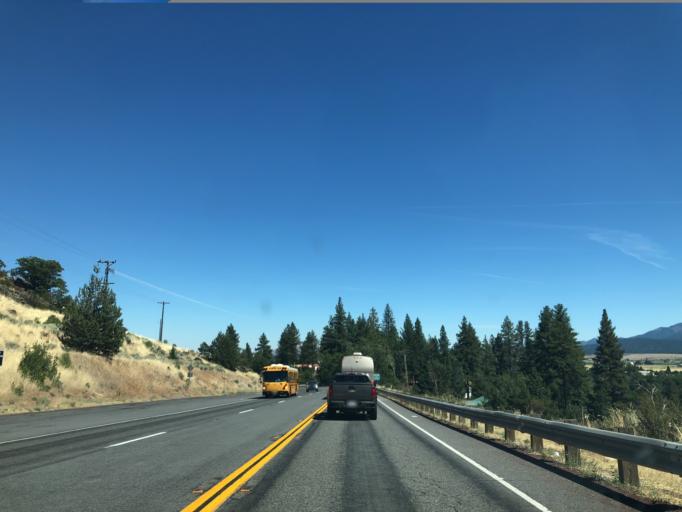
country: US
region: California
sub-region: Lassen County
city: Susanville
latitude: 40.4179
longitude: -120.6694
